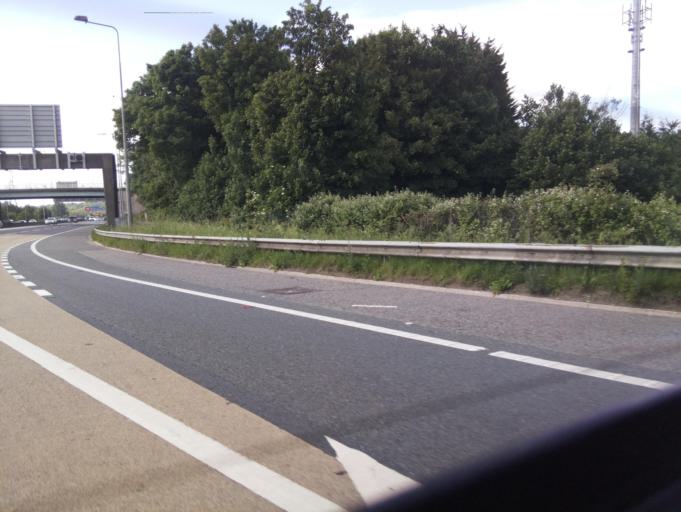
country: GB
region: England
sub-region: Manchester
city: Swinton
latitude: 53.4901
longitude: -2.3779
